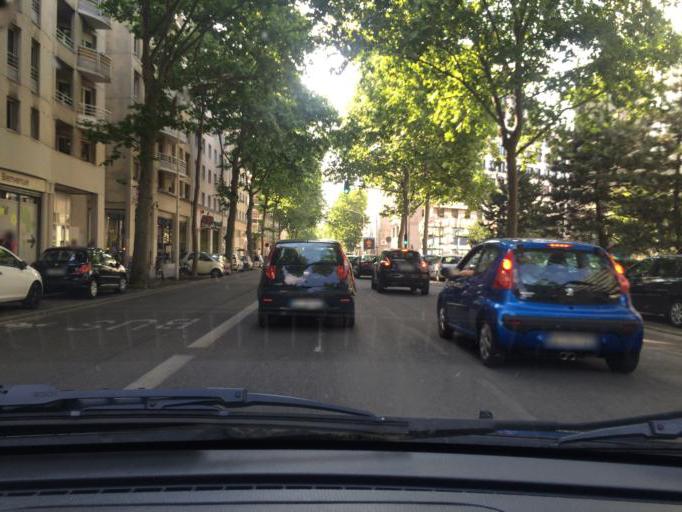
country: FR
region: Rhone-Alpes
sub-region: Departement du Rhone
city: Lyon
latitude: 45.7506
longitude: 4.8566
